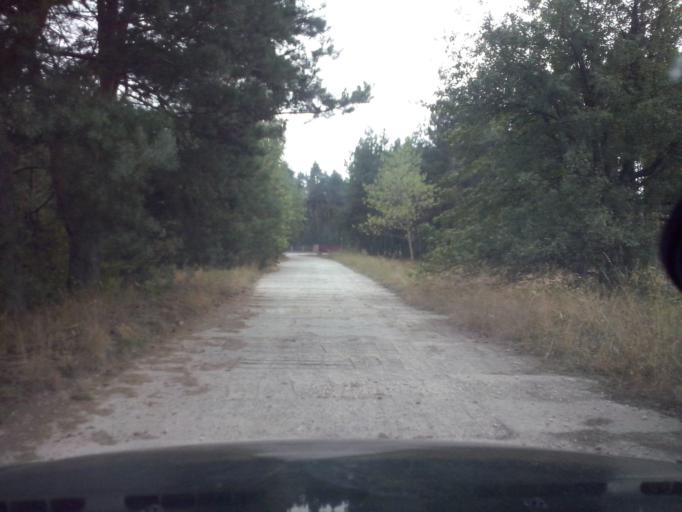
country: PL
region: Swietokrzyskie
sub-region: Powiat kielecki
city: Brzeziny
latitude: 50.7560
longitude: 20.5819
